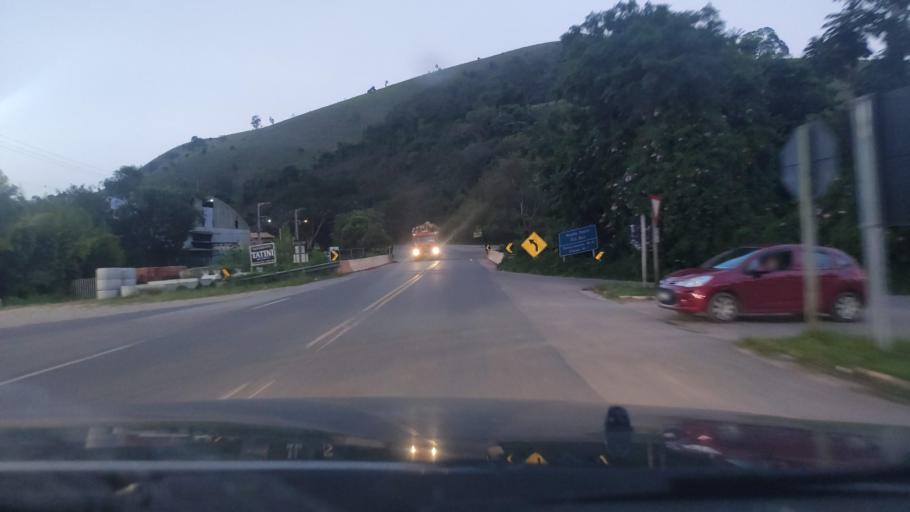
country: BR
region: Sao Paulo
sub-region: Campos Do Jordao
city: Campos do Jordao
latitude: -22.7435
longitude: -45.7394
